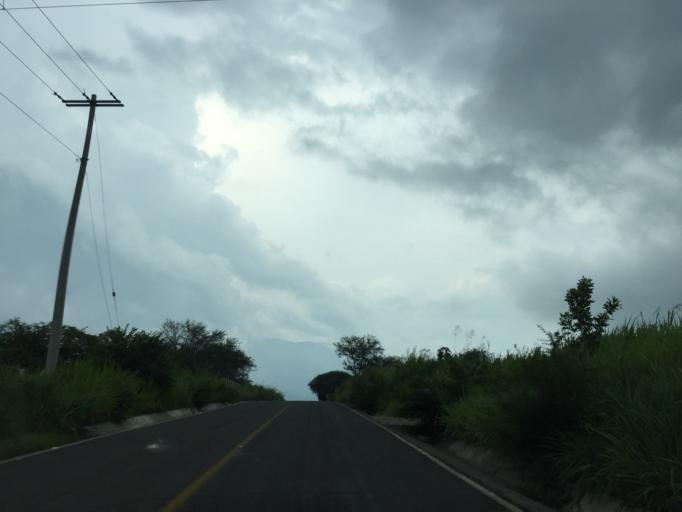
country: MX
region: Colima
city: Comala
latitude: 19.3334
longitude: -103.7669
